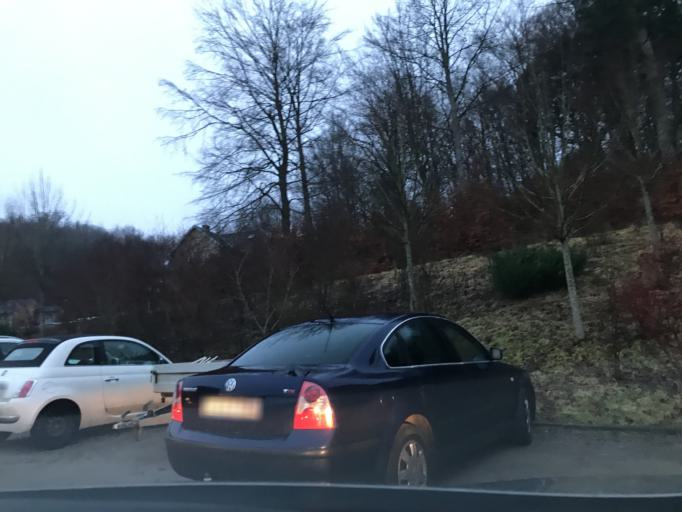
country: DK
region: South Denmark
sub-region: Vejle Kommune
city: Brejning
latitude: 55.6838
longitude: 9.7619
